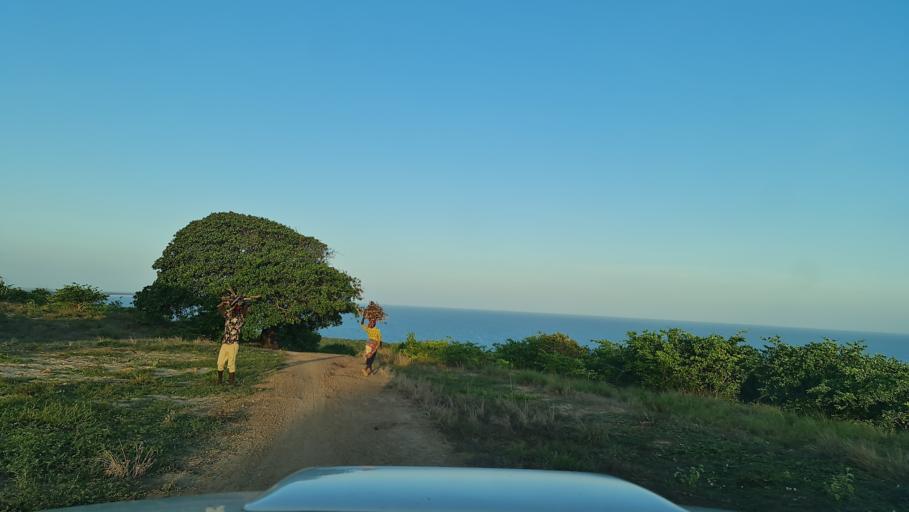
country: MZ
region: Nampula
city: Ilha de Mocambique
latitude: -15.6352
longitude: 40.4154
